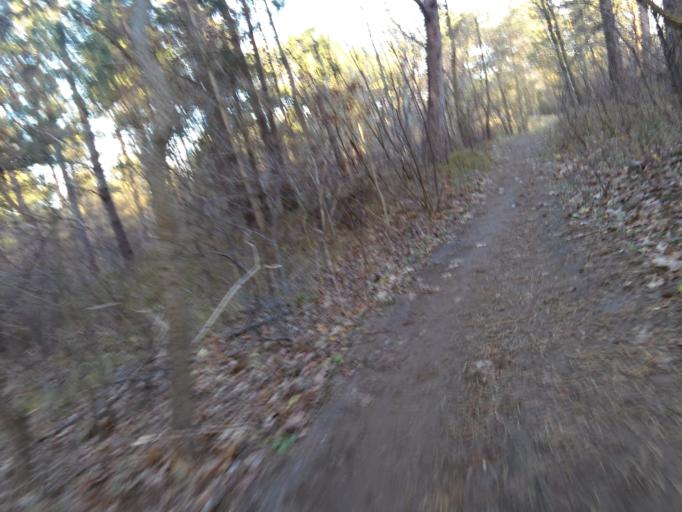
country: NL
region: South Holland
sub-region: Gemeente Noordwijkerhout
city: Noordwijkerhout
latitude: 52.2679
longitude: 4.4606
